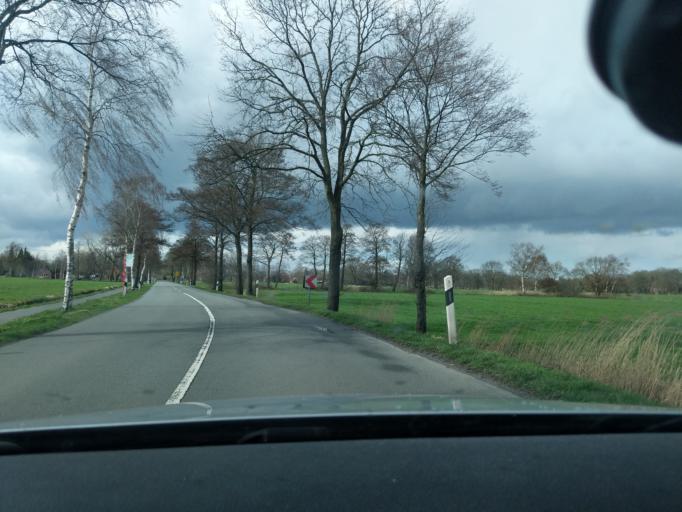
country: DE
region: Lower Saxony
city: Stade
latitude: 53.6252
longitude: 9.4384
